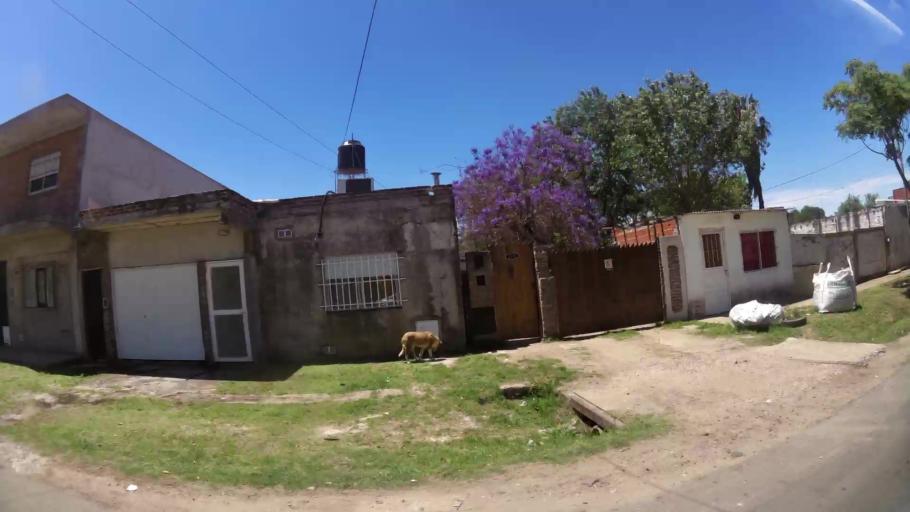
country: AR
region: Santa Fe
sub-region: Departamento de Rosario
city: Rosario
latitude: -32.9570
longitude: -60.7050
